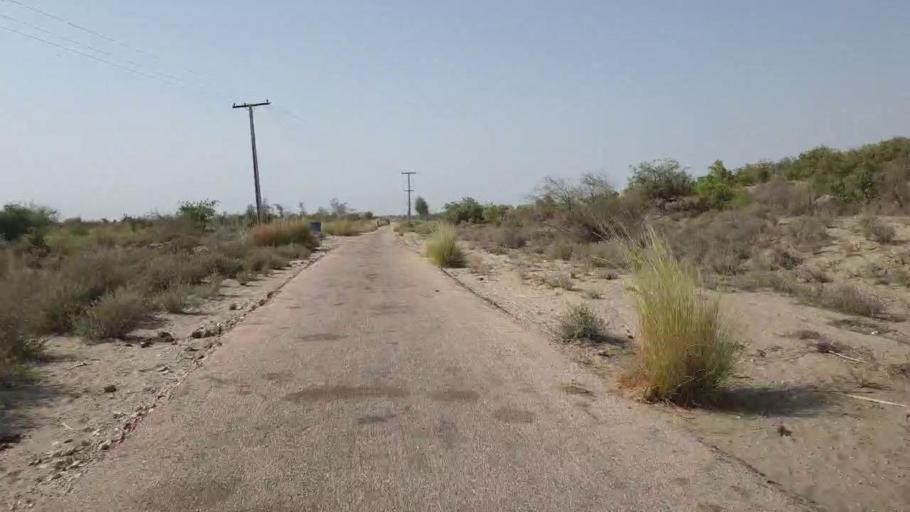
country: PK
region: Sindh
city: Jam Sahib
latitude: 26.5791
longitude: 68.9209
